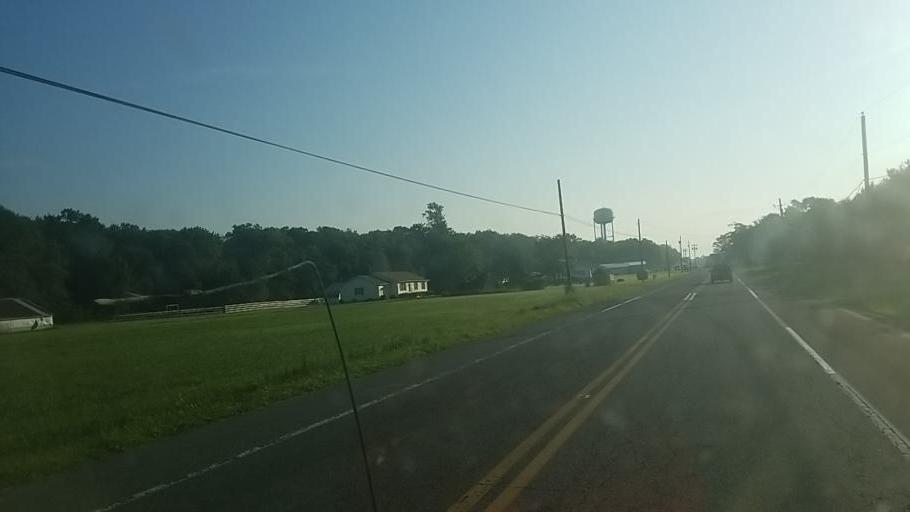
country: US
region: Maryland
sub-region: Worcester County
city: Ocean Pines
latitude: 38.4655
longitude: -75.1230
